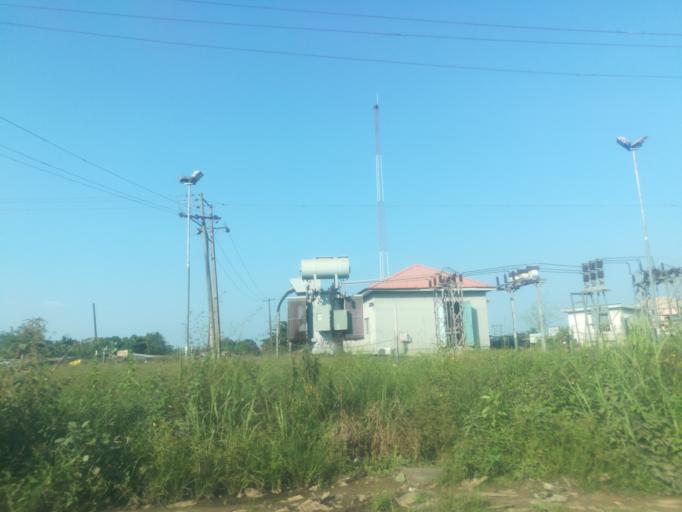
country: NG
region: Ogun
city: Abeokuta
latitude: 7.1818
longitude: 3.2802
